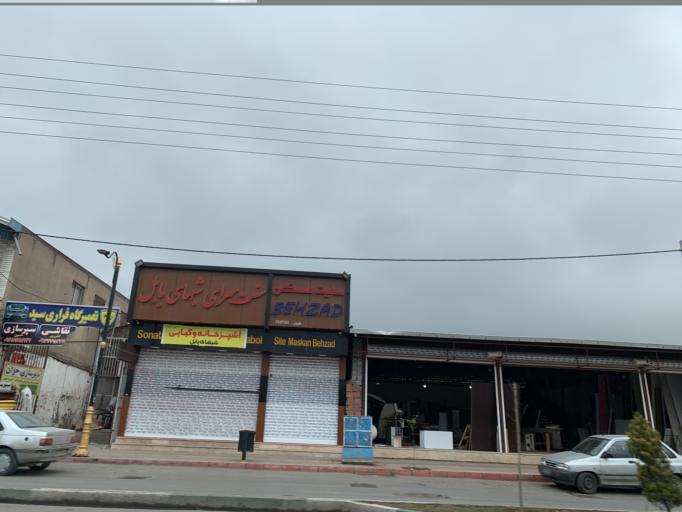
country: IR
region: Mazandaran
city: Babol
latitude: 36.5338
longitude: 52.6486
